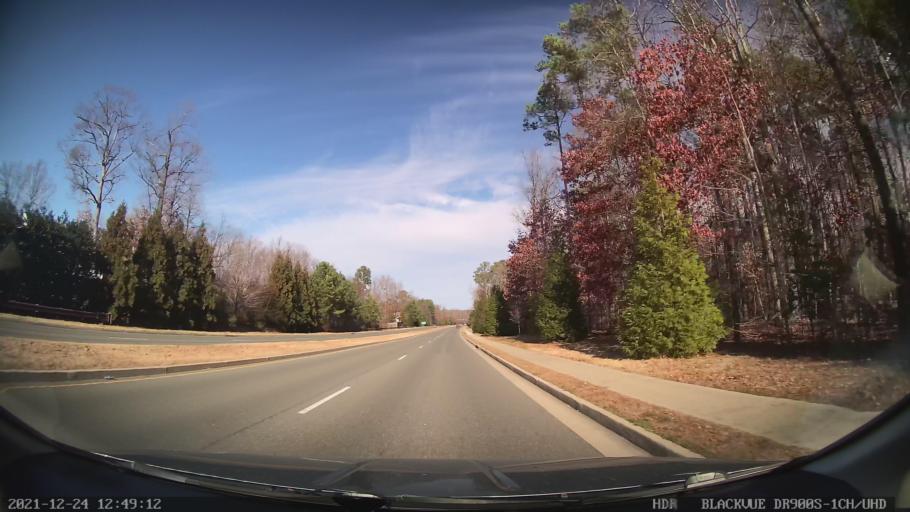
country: US
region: Virginia
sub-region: Henrico County
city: Short Pump
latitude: 37.6395
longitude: -77.6122
